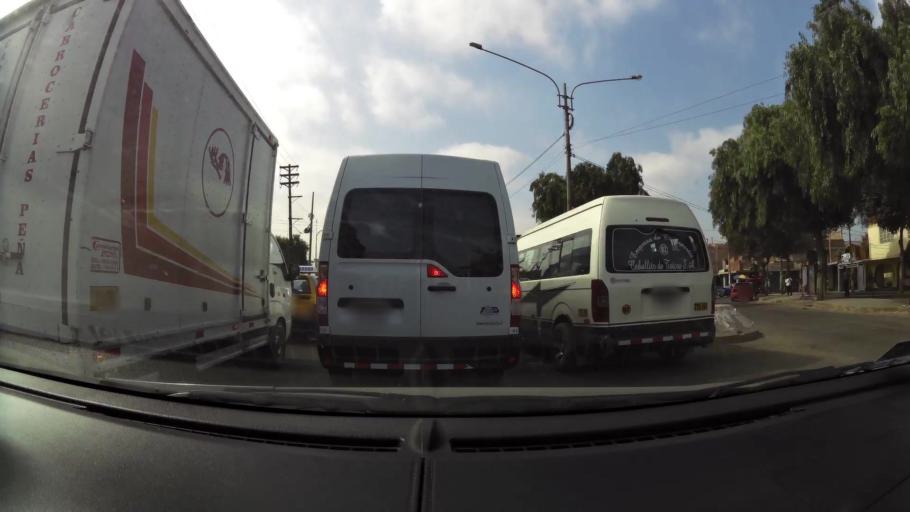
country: PE
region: La Libertad
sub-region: Provincia de Trujillo
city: Trujillo
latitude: -8.1064
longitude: -79.0109
